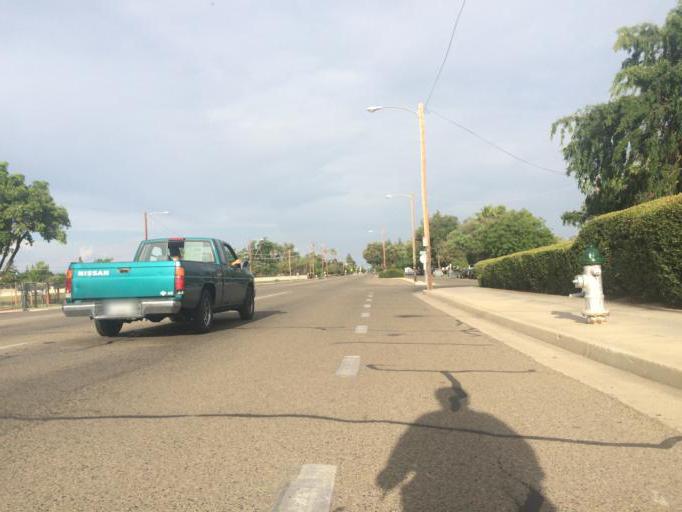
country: US
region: California
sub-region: Fresno County
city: Fresno
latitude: 36.8157
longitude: -119.7703
